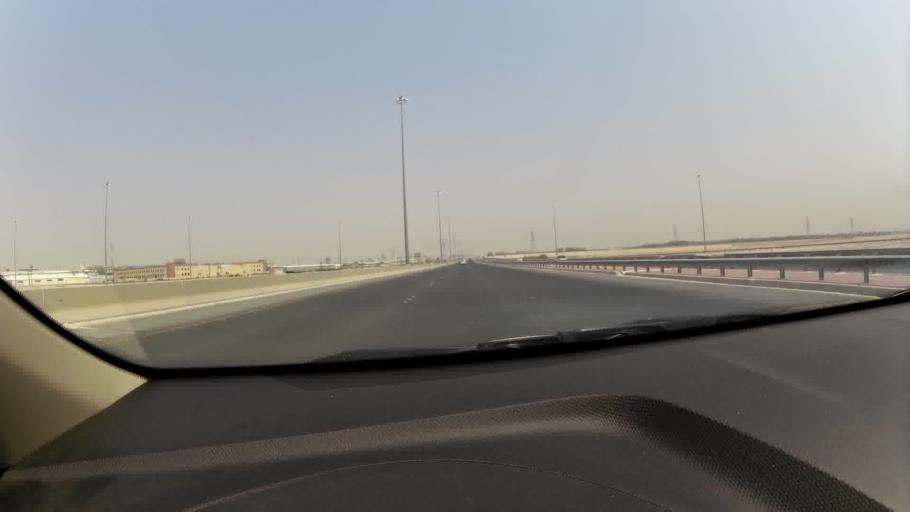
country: KW
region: Muhafazat al Jahra'
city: Al Jahra'
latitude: 29.2953
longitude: 47.7356
